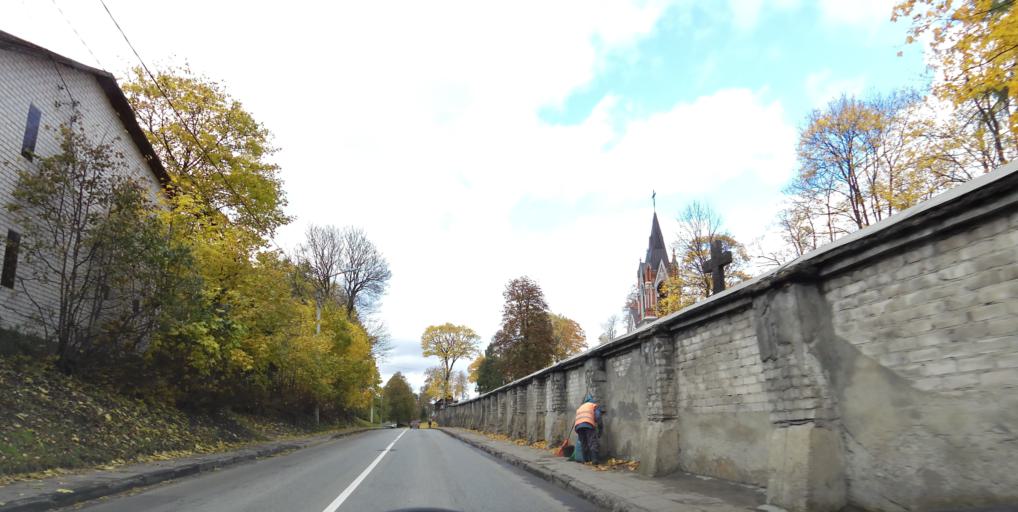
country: LT
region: Vilnius County
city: Rasos
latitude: 54.6684
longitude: 25.3032
